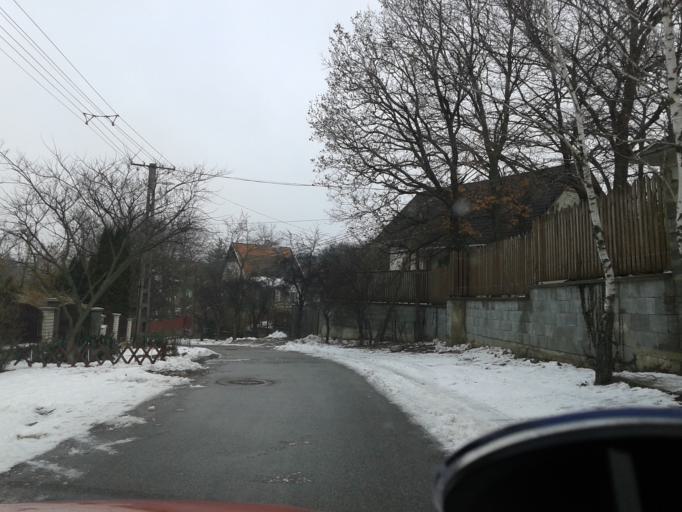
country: HU
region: Pest
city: Erd
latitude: 47.4077
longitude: 18.9273
